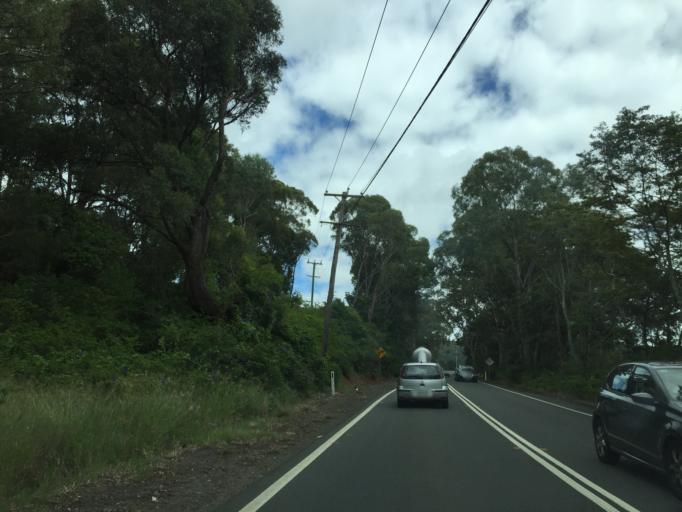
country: AU
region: New South Wales
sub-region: Hawkesbury
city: Richmond
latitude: -33.5475
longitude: 150.6516
